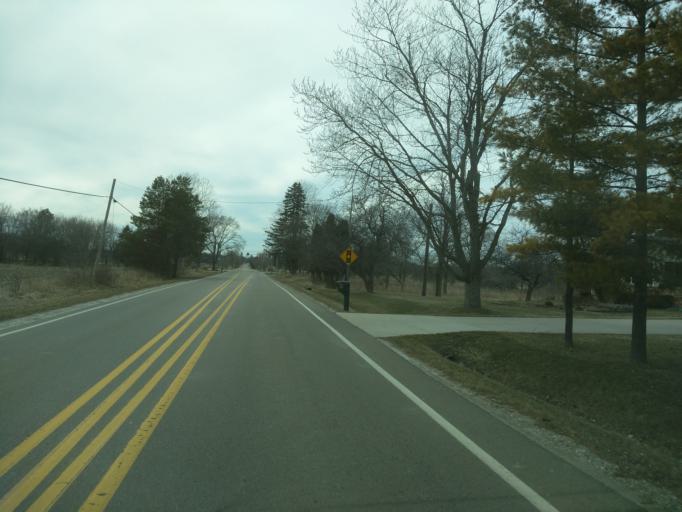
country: US
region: Michigan
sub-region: Ingham County
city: Okemos
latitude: 42.6693
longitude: -84.4304
